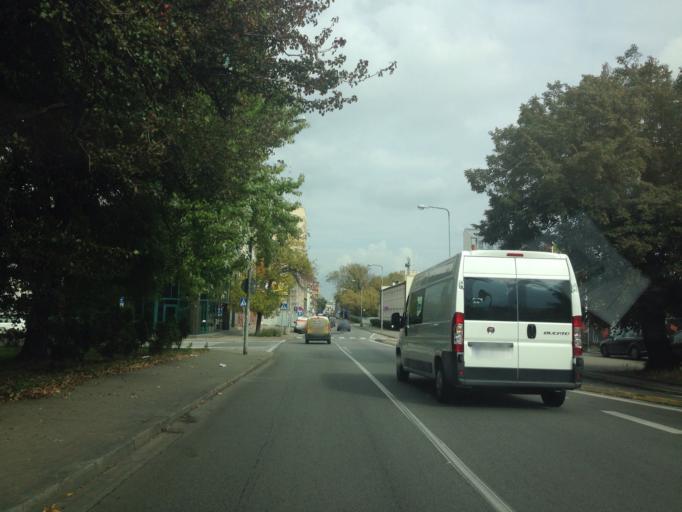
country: PL
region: Masovian Voivodeship
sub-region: Warszawa
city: Praga Polnoc
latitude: 52.2485
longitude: 21.0291
